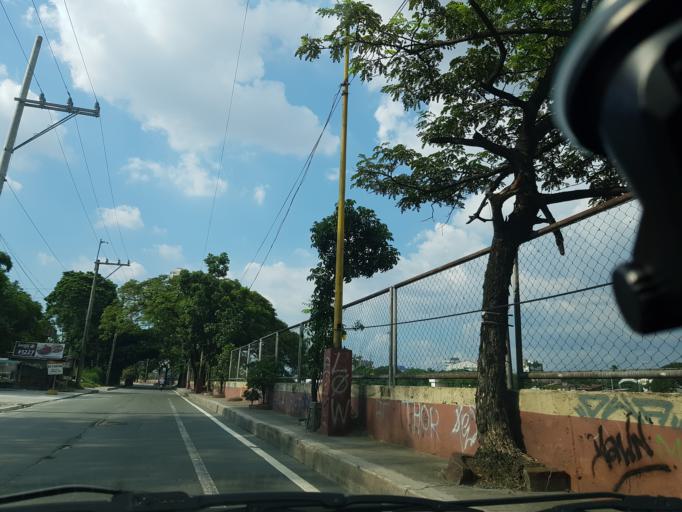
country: PH
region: Metro Manila
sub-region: Marikina
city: Calumpang
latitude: 14.5951
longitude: 121.0908
